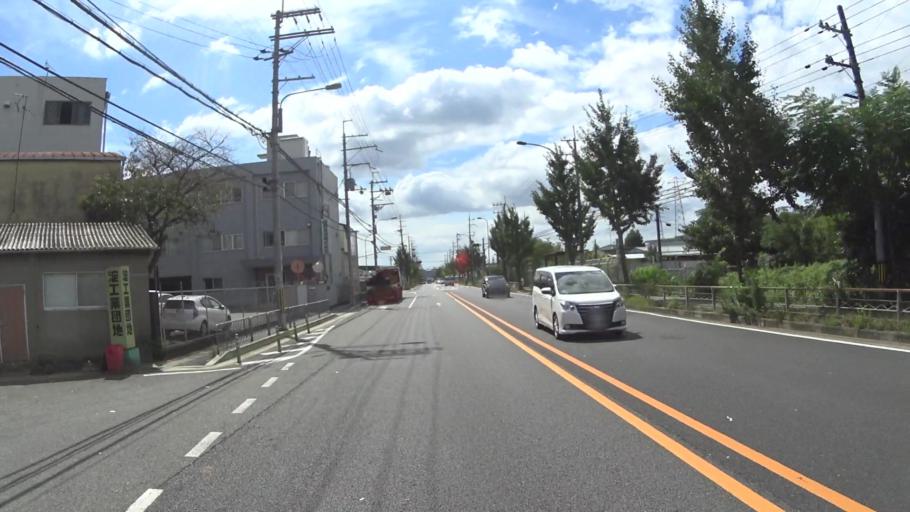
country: JP
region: Kyoto
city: Muko
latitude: 34.9211
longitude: 135.7327
